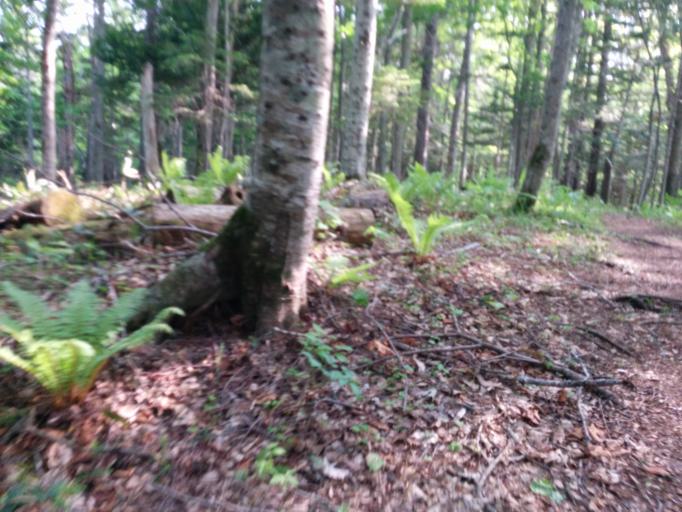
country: JP
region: Hokkaido
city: Bihoro
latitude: 43.4374
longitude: 144.1036
